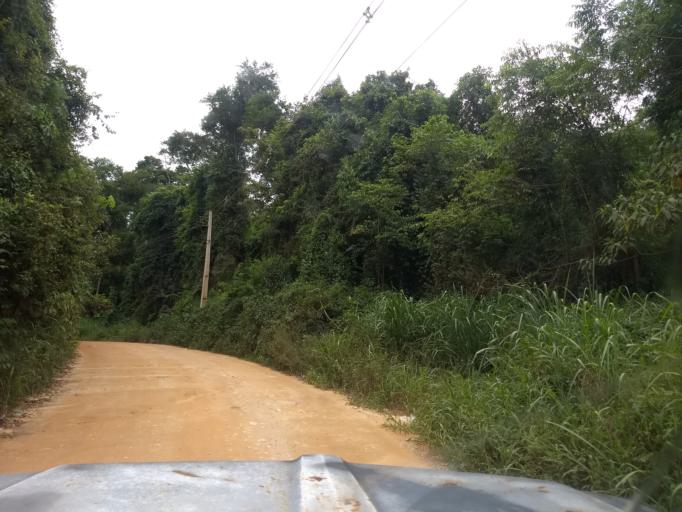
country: BR
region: Sao Paulo
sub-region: Cabreuva
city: Cabreuva
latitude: -23.4171
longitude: -47.1953
